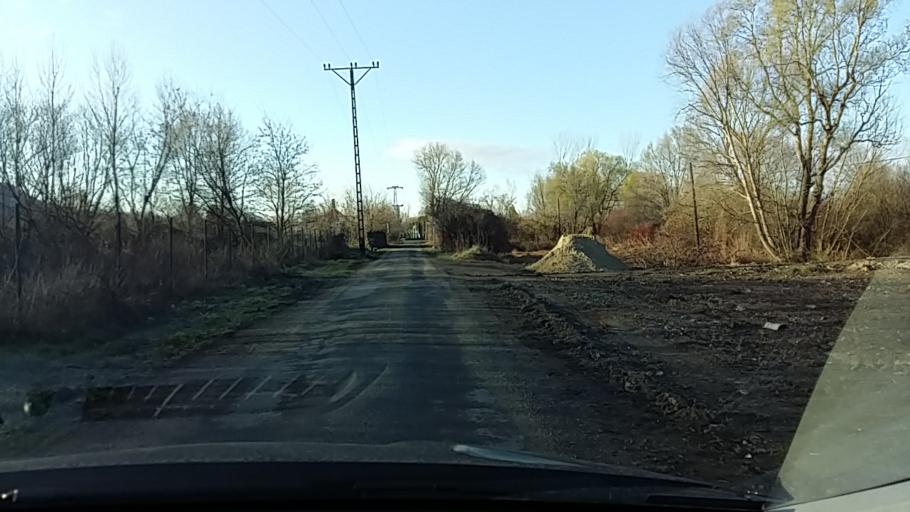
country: HU
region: Veszprem
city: Tapolca
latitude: 46.8754
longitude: 17.4387
